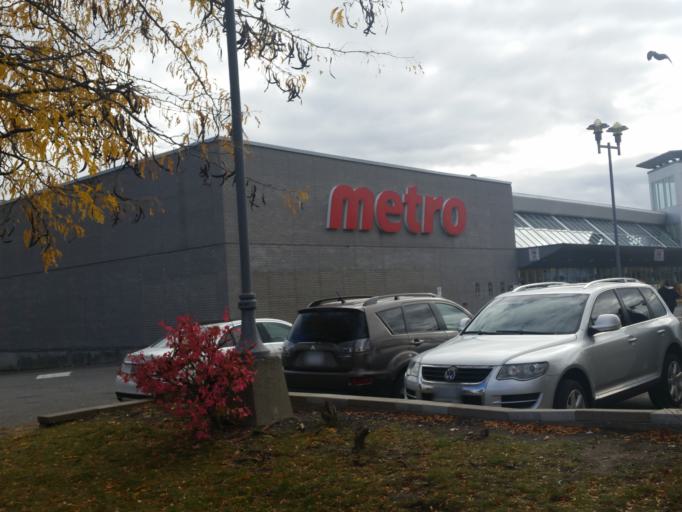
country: CA
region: Ontario
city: Ottawa
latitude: 45.4400
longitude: -75.6755
